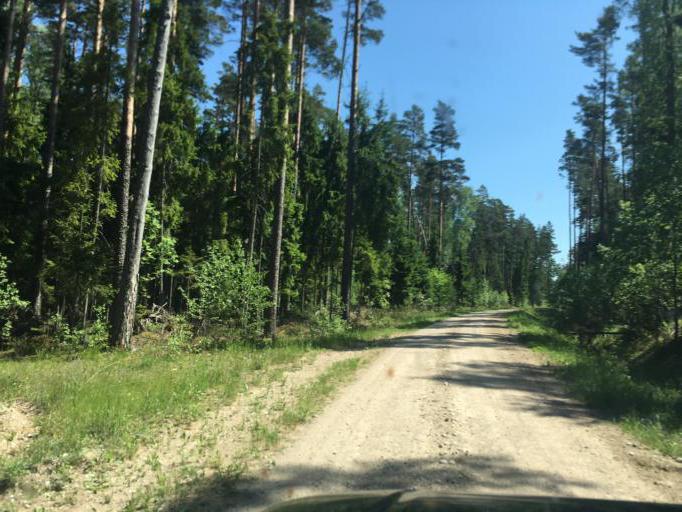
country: LV
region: Talsu Rajons
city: Valdemarpils
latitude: 57.4402
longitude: 22.6728
